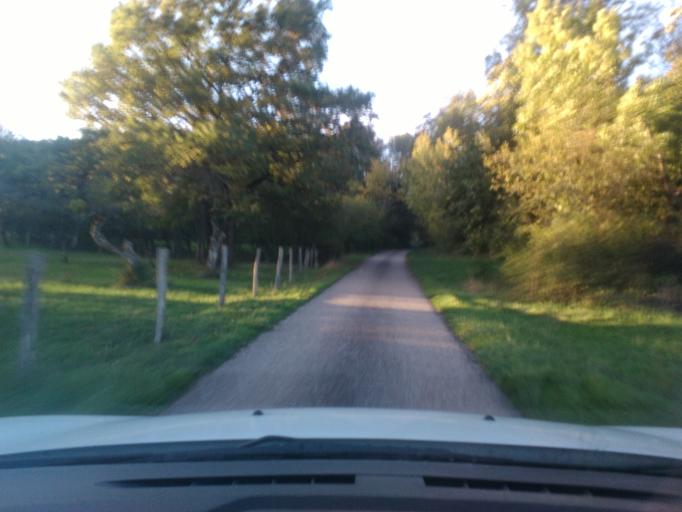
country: FR
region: Lorraine
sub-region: Departement des Vosges
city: Charmes
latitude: 48.3361
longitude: 6.2641
